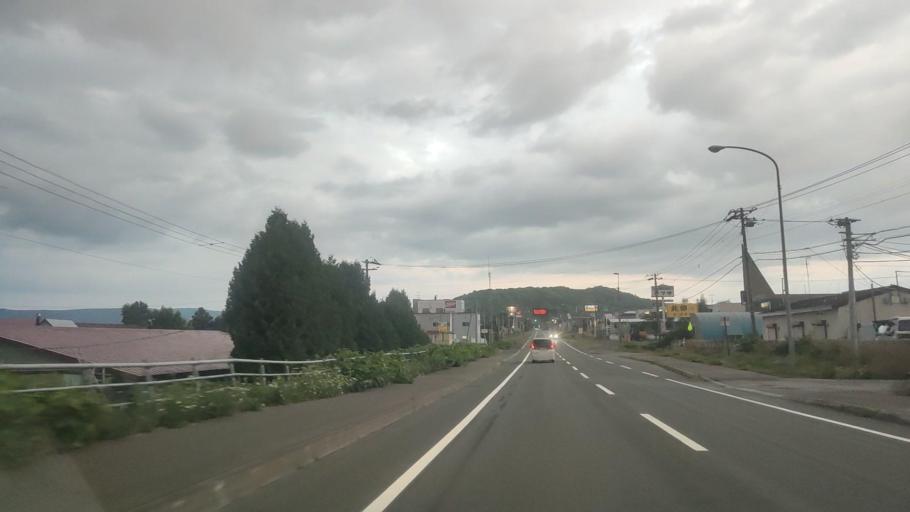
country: JP
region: Hokkaido
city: Shimo-furano
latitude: 43.3510
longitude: 142.3666
